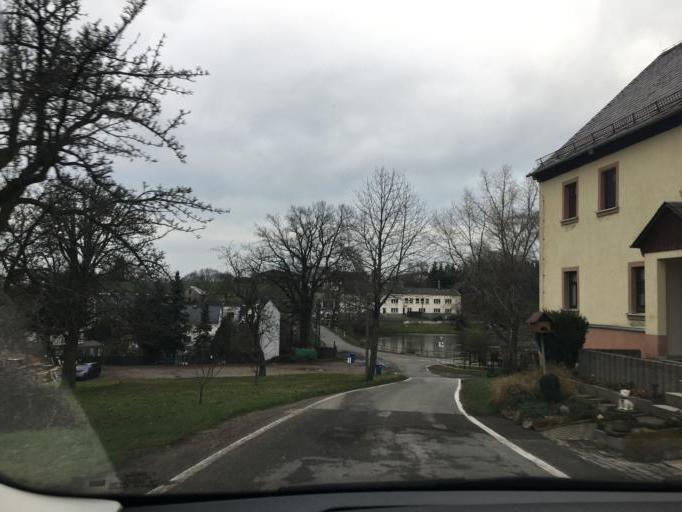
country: DE
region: Saxony
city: Niederfrohna
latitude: 50.8700
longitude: 12.6975
